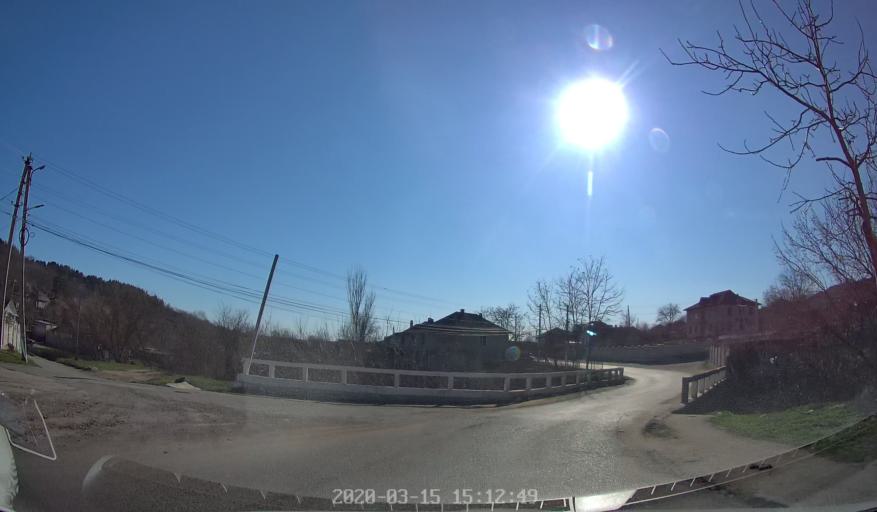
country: MD
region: Orhei
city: Orhei
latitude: 47.2527
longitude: 28.7737
